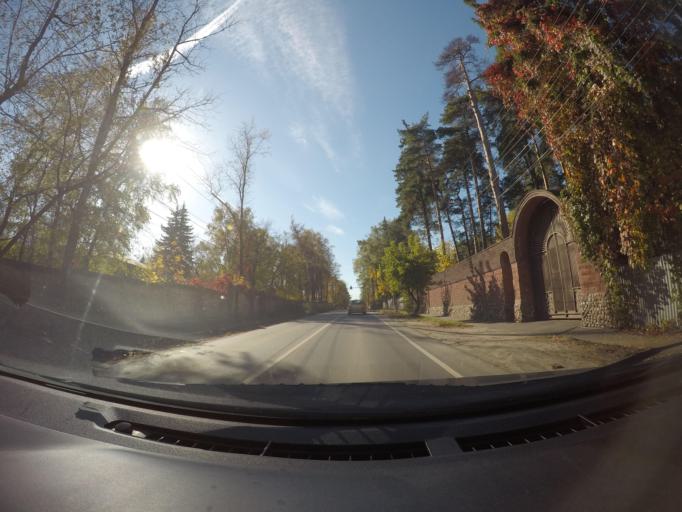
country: RU
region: Moskovskaya
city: Rodniki
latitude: 55.6369
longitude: 38.0528
